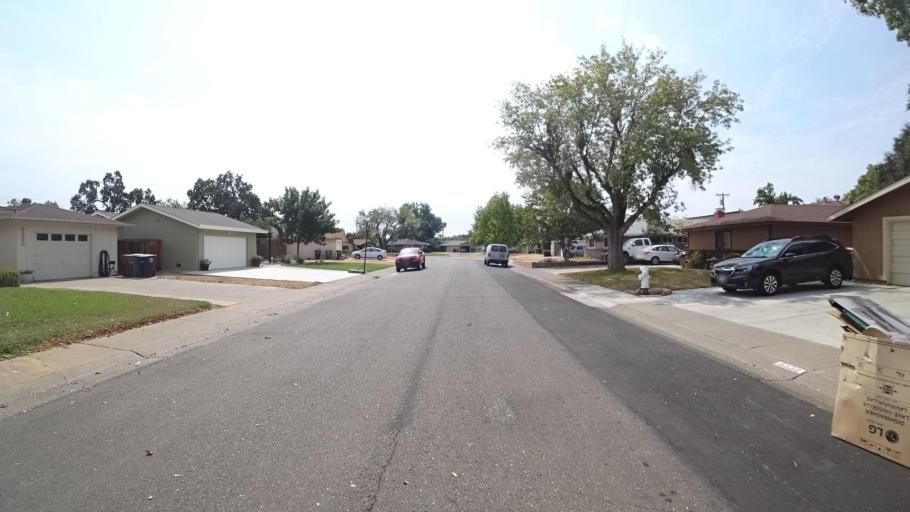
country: US
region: California
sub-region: Sacramento County
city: Elk Grove
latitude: 38.4181
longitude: -121.3739
